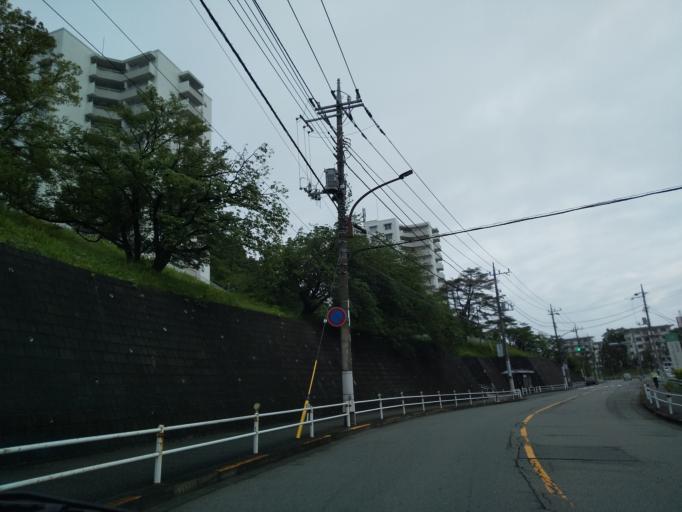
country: JP
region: Tokyo
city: Hino
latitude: 35.6486
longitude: 139.4183
